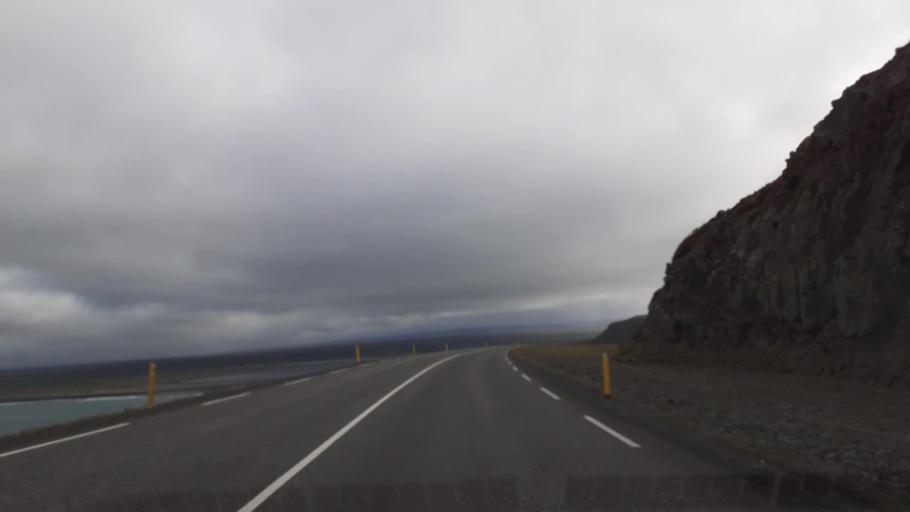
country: IS
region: Northeast
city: Husavik
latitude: 66.1356
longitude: -16.9509
